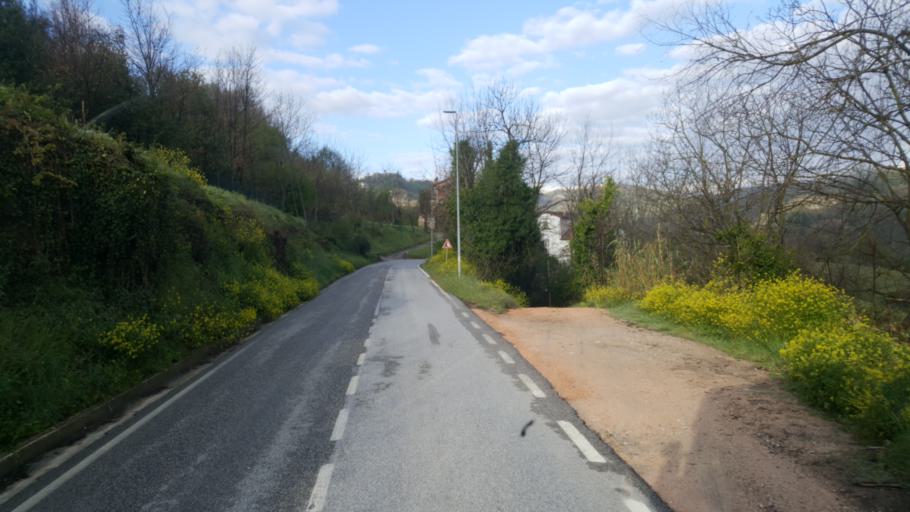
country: IT
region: The Marches
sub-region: Provincia di Ascoli Piceno
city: Venarotta
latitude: 42.8723
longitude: 13.5445
